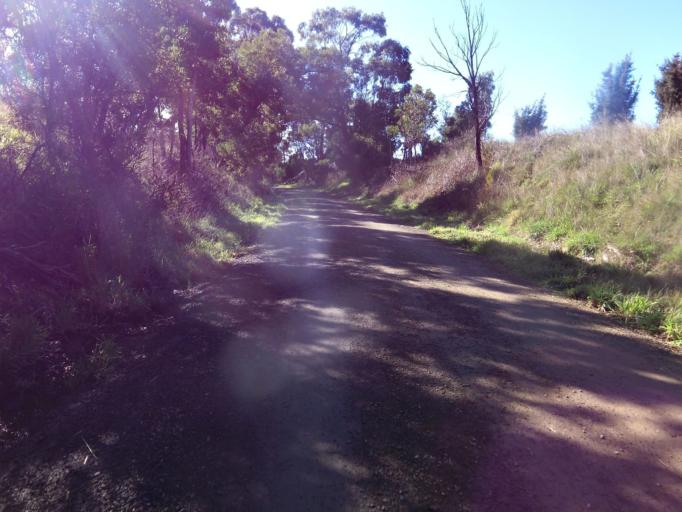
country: AU
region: Victoria
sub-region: Yarra Ranges
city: Lilydale
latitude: -37.7319
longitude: 145.3705
